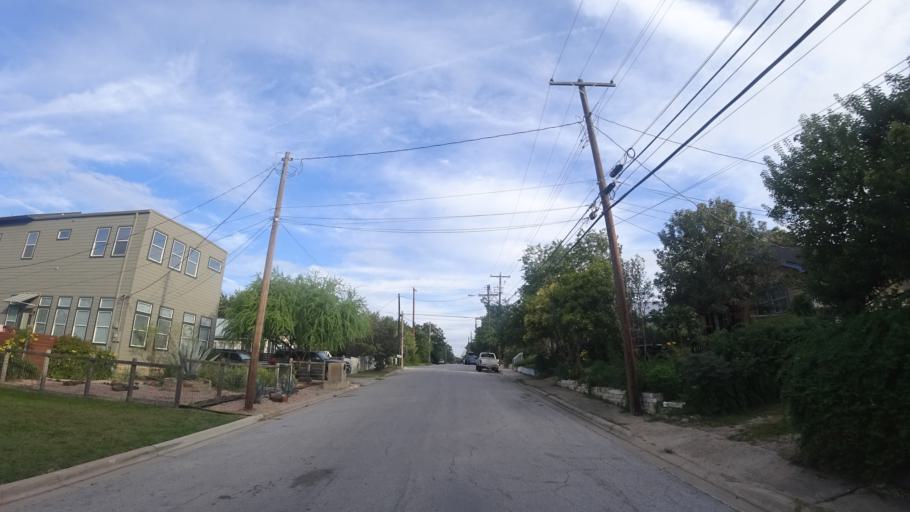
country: US
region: Texas
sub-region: Travis County
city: Austin
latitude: 30.2775
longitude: -97.7126
